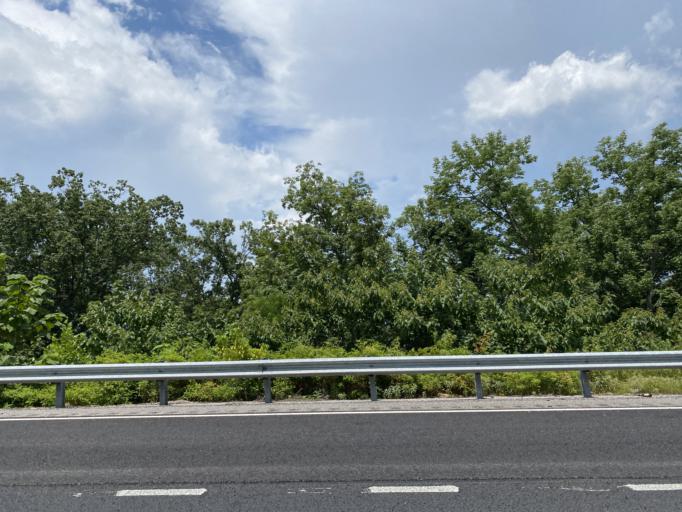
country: US
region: Alabama
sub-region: Madison County
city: Huntsville
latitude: 34.7044
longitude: -86.5197
